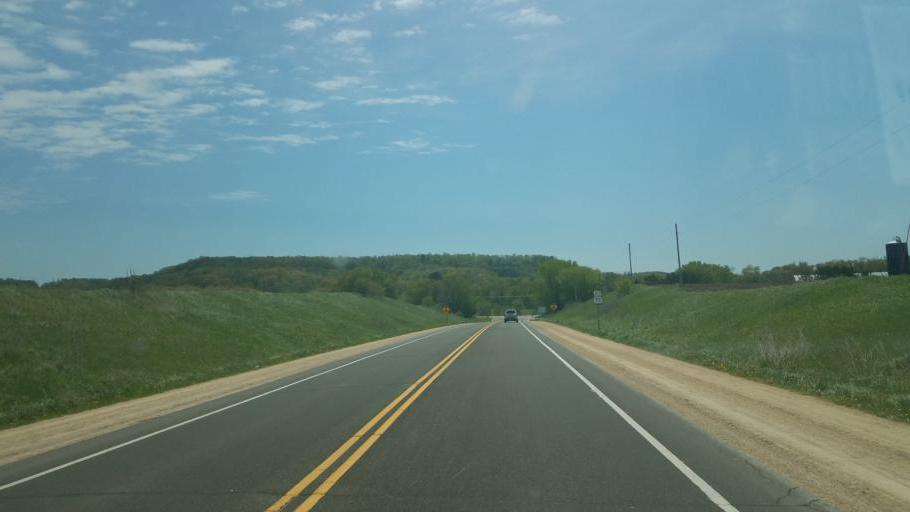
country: US
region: Wisconsin
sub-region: Monroe County
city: Tomah
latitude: 43.8361
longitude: -90.4740
